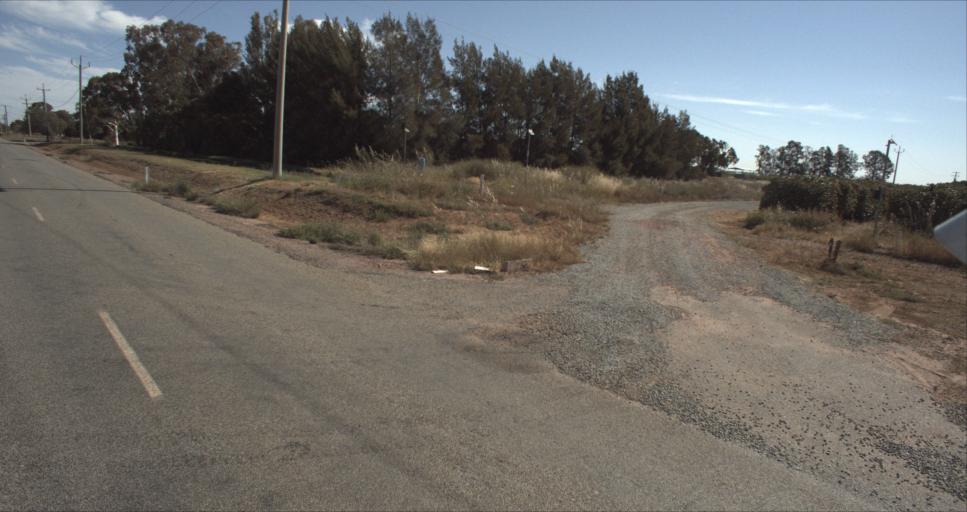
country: AU
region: New South Wales
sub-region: Leeton
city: Leeton
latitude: -34.5616
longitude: 146.3835
